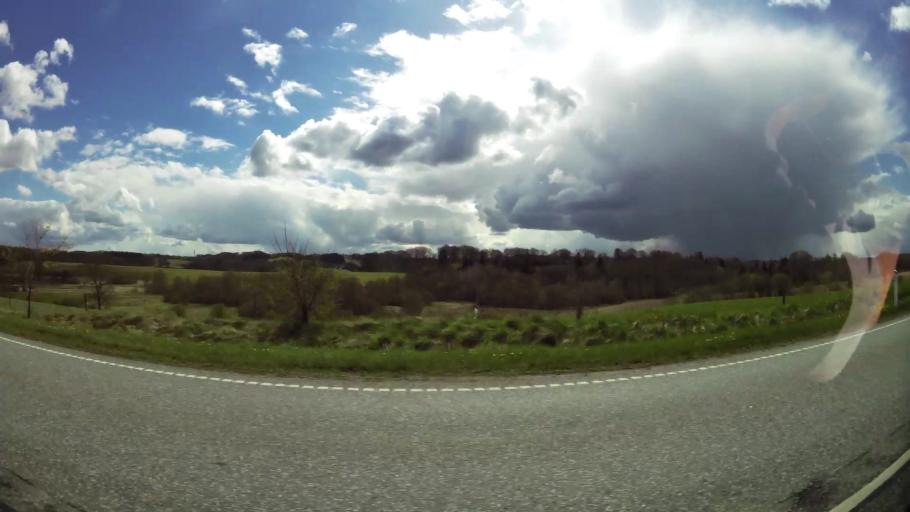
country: DK
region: South Denmark
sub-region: Vejle Kommune
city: Jelling
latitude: 55.6980
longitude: 9.4107
